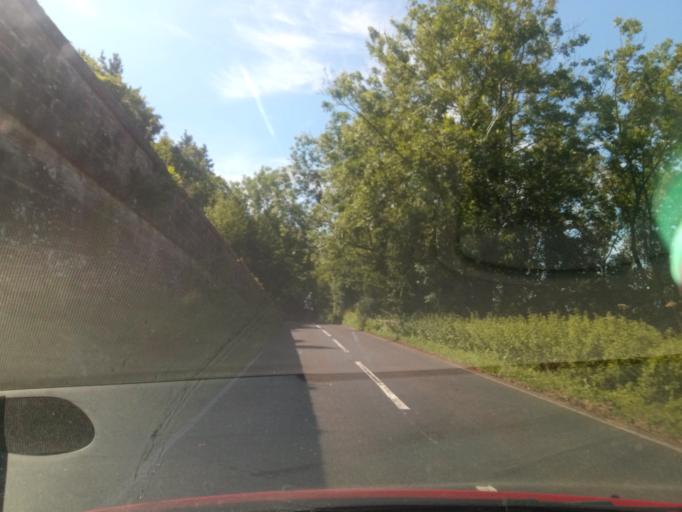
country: GB
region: England
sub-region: Northumberland
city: Bardon Mill
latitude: 54.9309
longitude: -2.3047
